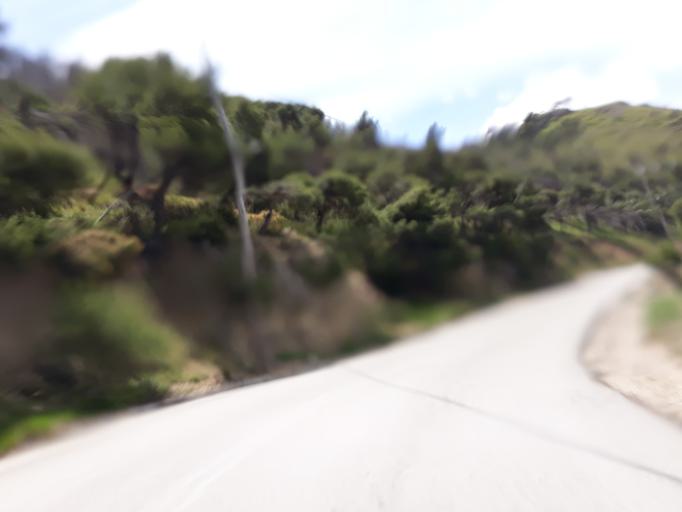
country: GR
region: Attica
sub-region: Nomarchia Dytikis Attikis
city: Magoula
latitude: 38.1655
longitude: 23.5442
